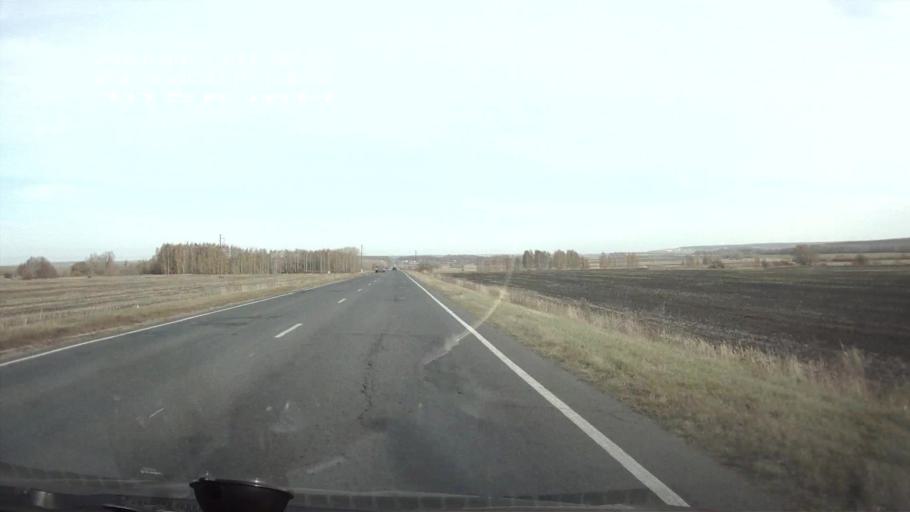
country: RU
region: Mordoviya
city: Atyashevo
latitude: 54.5421
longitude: 45.9379
